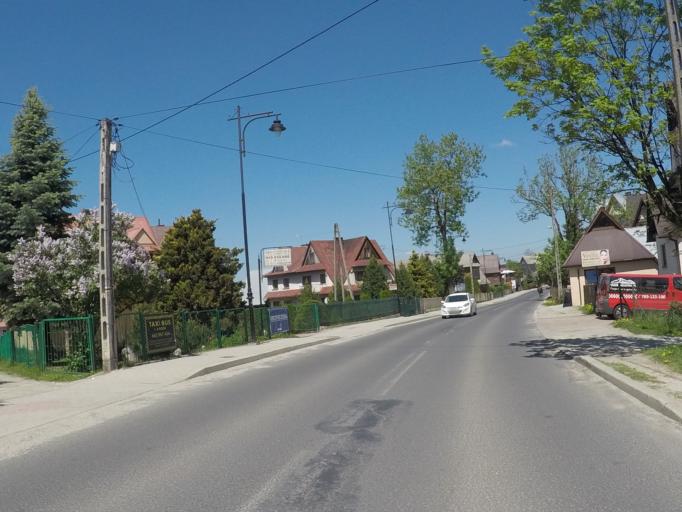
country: PL
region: Lesser Poland Voivodeship
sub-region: Powiat tatrzanski
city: Bukowina Tatrzanska
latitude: 49.3380
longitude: 20.0997
